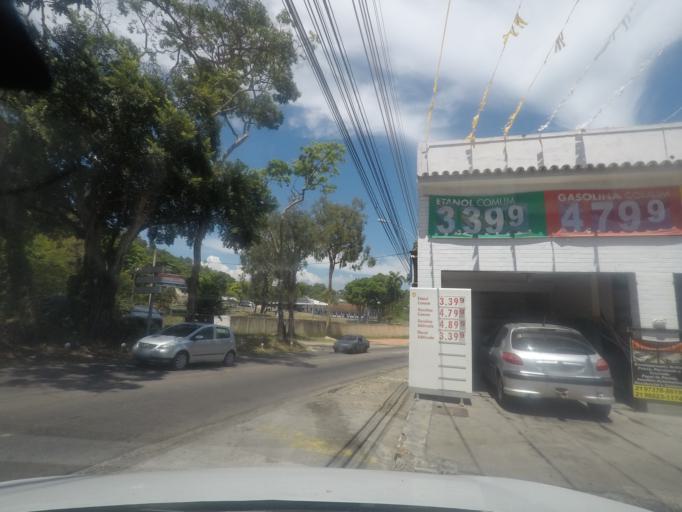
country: BR
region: Rio de Janeiro
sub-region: Itaguai
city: Itaguai
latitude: -22.9997
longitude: -43.6434
